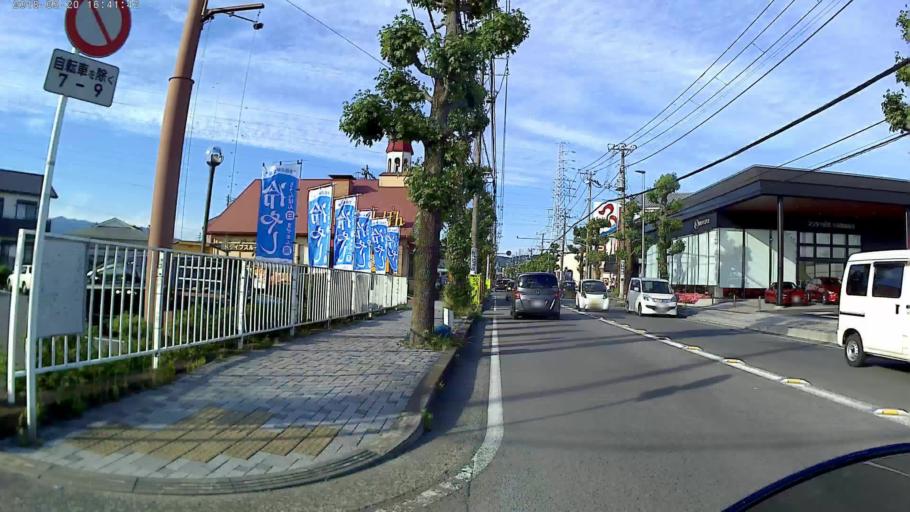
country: JP
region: Kanagawa
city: Odawara
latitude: 35.2769
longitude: 139.1659
